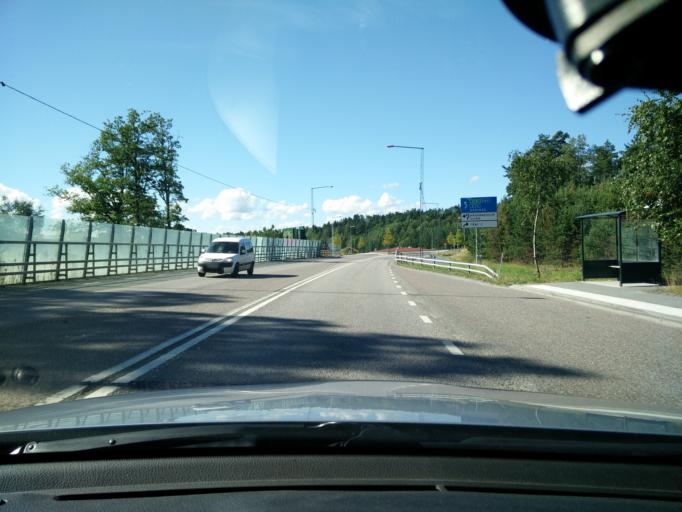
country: SE
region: Stockholm
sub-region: Taby Kommun
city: Taby
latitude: 59.4738
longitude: 18.1195
